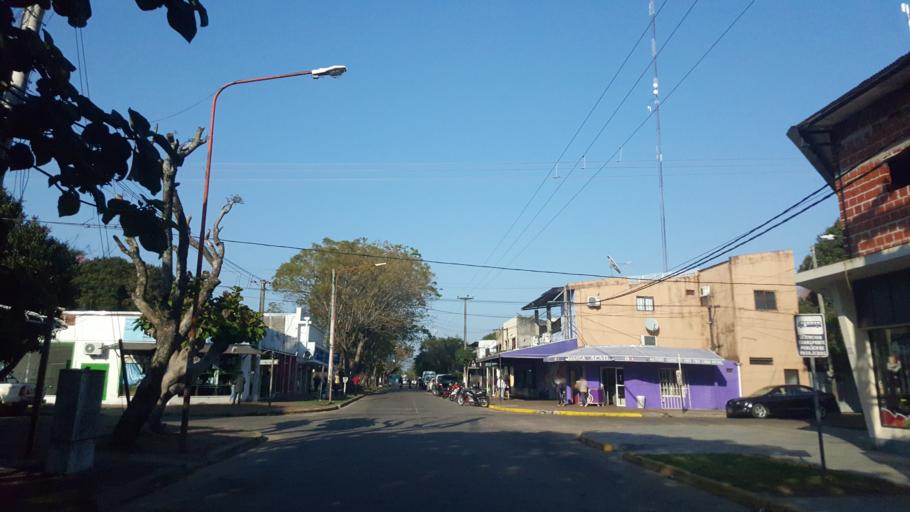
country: AR
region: Corrientes
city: Ituzaingo
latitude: -27.5822
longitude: -56.6847
